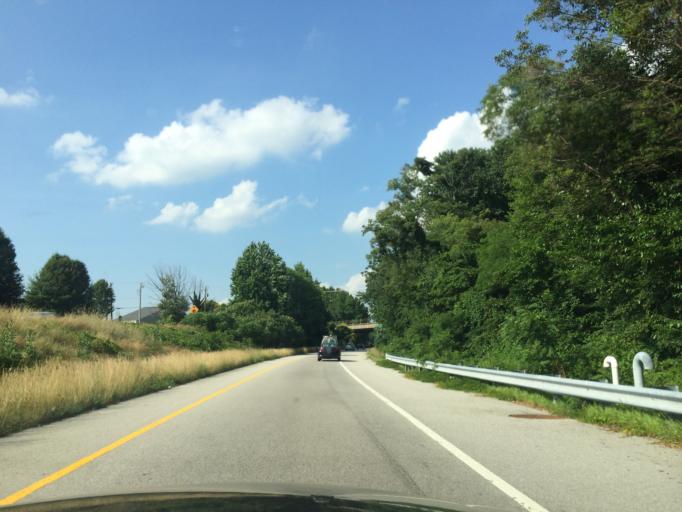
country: US
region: Maryland
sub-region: Howard County
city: Ellicott City
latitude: 39.2770
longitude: -76.8165
